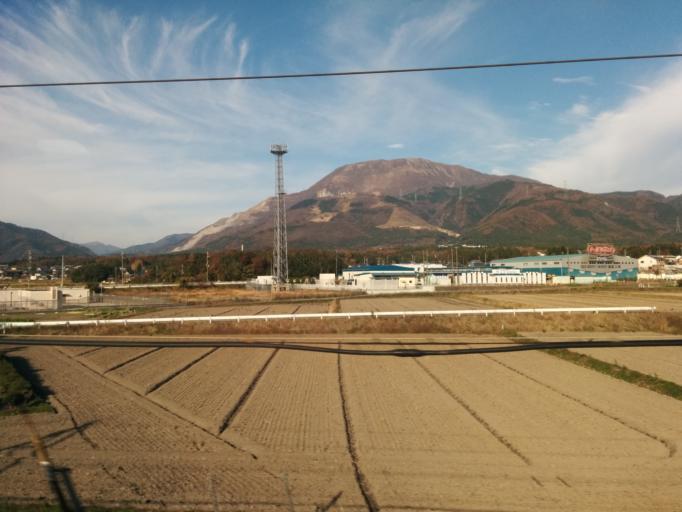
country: JP
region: Shiga Prefecture
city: Nagahama
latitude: 35.3651
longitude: 136.3855
